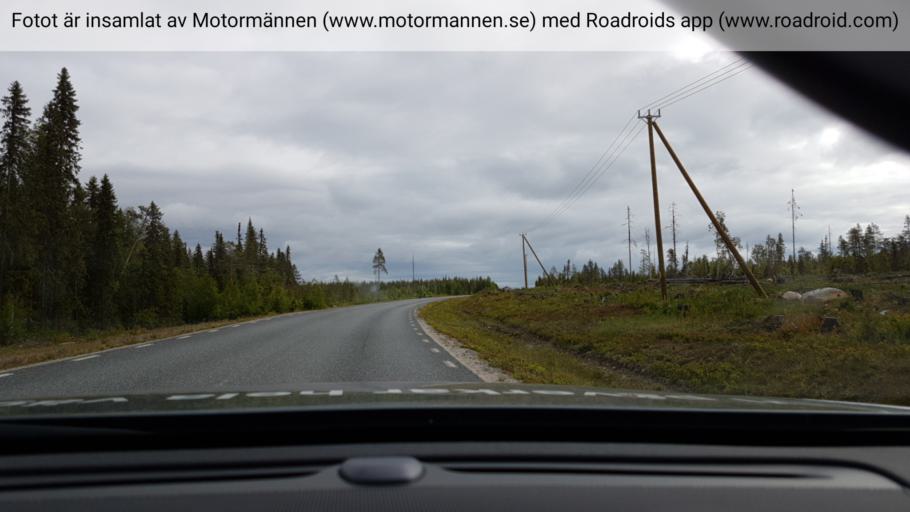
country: SE
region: Vaesterbotten
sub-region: Asele Kommun
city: Insjon
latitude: 64.2850
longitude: 17.6175
